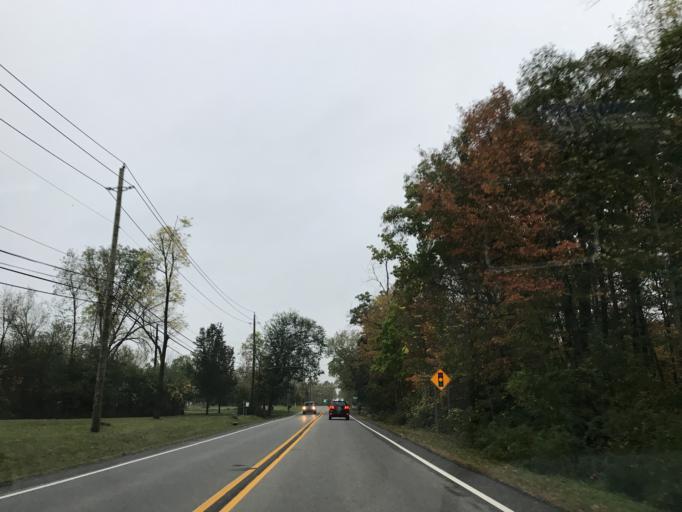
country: US
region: Michigan
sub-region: Oakland County
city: Franklin
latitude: 42.4737
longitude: -83.3183
